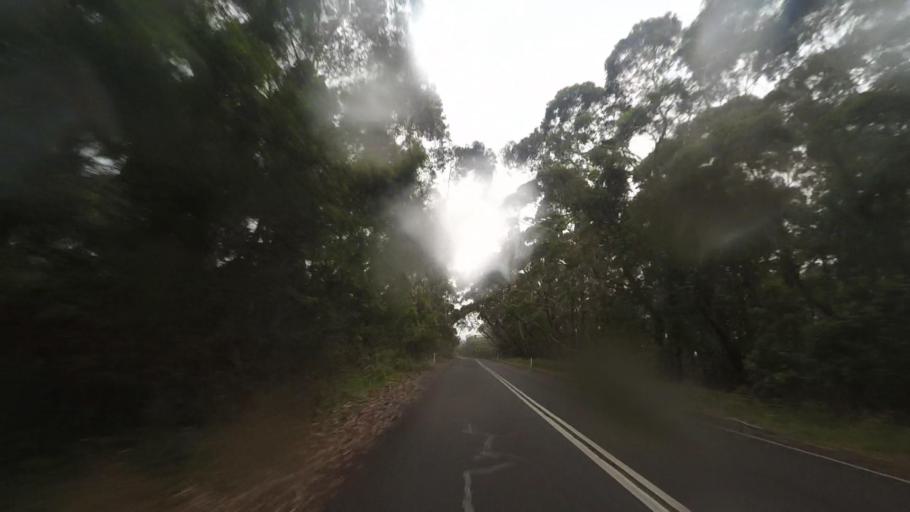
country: AU
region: New South Wales
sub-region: Wollongong
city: Mount Keira
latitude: -34.4008
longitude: 150.8402
